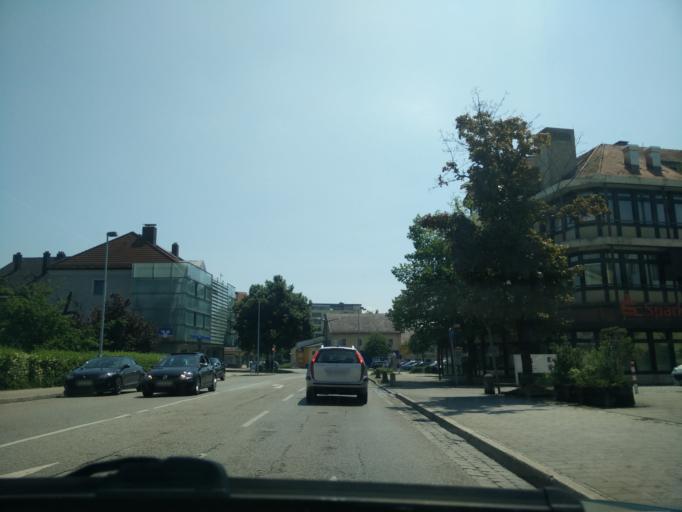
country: DE
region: Bavaria
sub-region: Upper Bavaria
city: Freilassing
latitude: 47.8414
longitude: 12.9816
